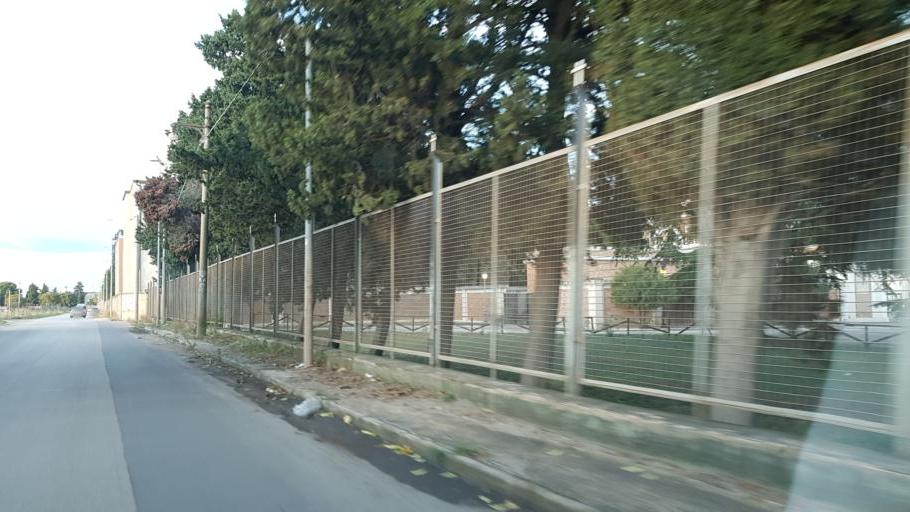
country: IT
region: Apulia
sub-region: Provincia di Foggia
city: Foggia
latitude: 41.4725
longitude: 15.5478
